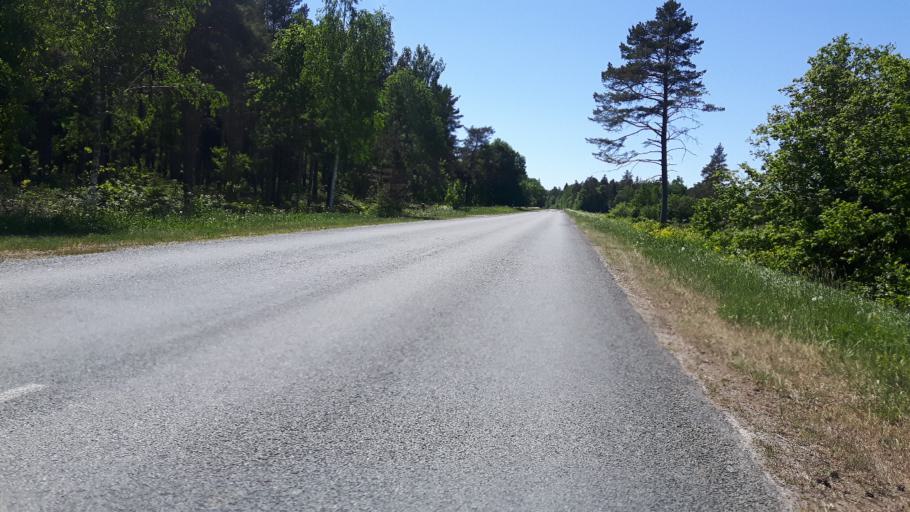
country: EE
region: Harju
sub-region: Kuusalu vald
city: Kuusalu
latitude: 59.4768
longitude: 25.4609
